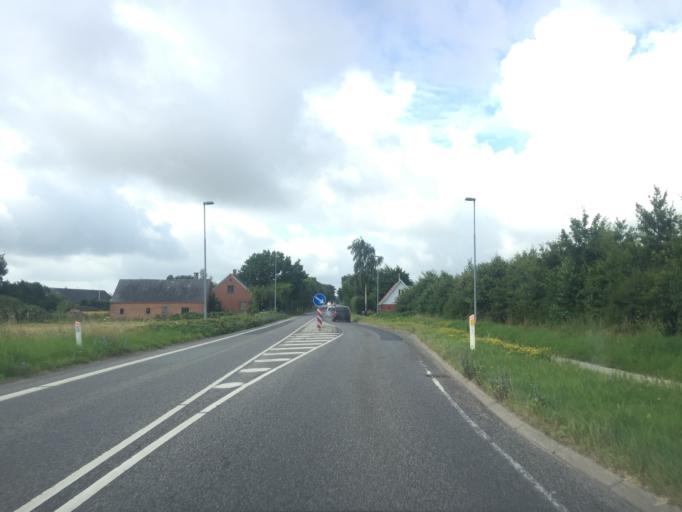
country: DK
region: South Denmark
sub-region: Svendborg Kommune
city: Thuro By
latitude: 55.0930
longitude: 10.6977
